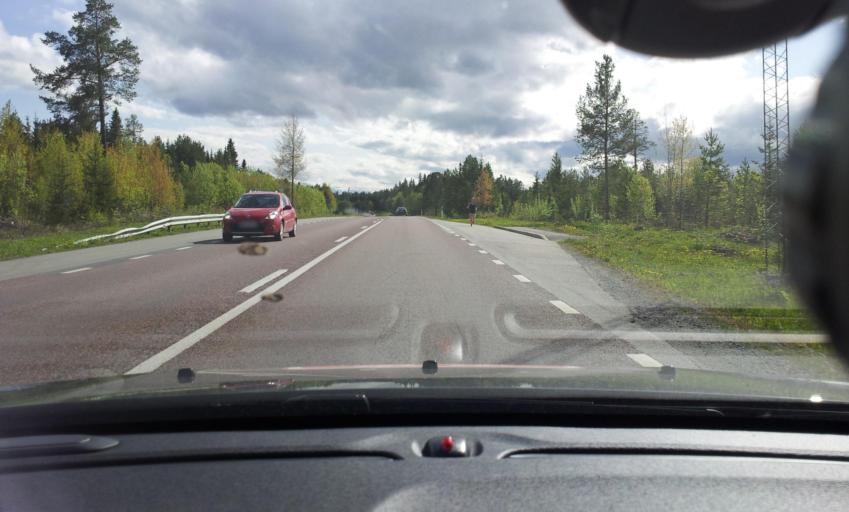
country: SE
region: Jaemtland
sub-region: OEstersunds Kommun
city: Brunflo
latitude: 63.0538
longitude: 14.8287
